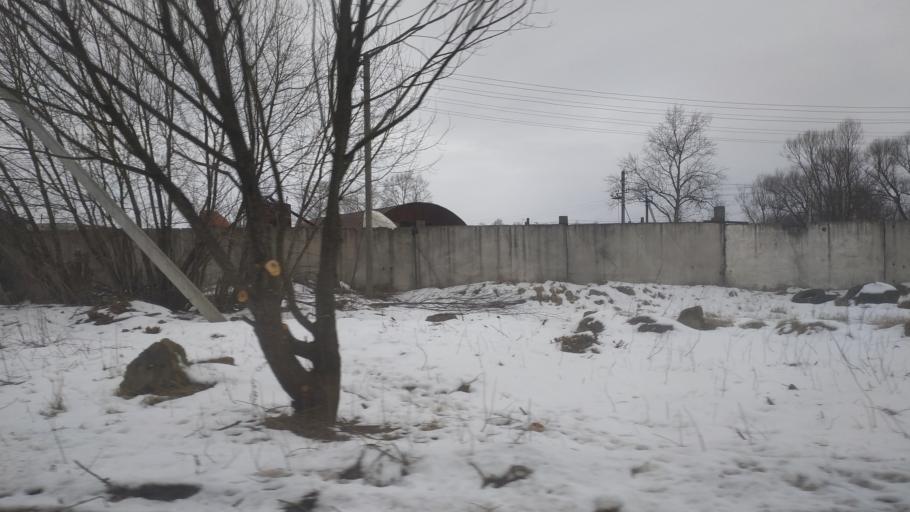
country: RU
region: Tverskaya
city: Tver
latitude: 56.8949
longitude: 35.8437
